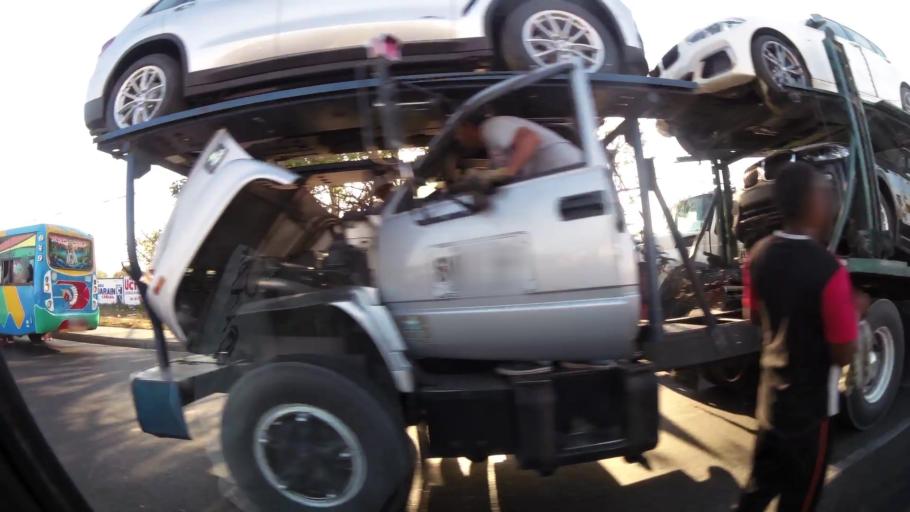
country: CO
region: Atlantico
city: Soledad
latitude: 10.9155
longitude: -74.7741
